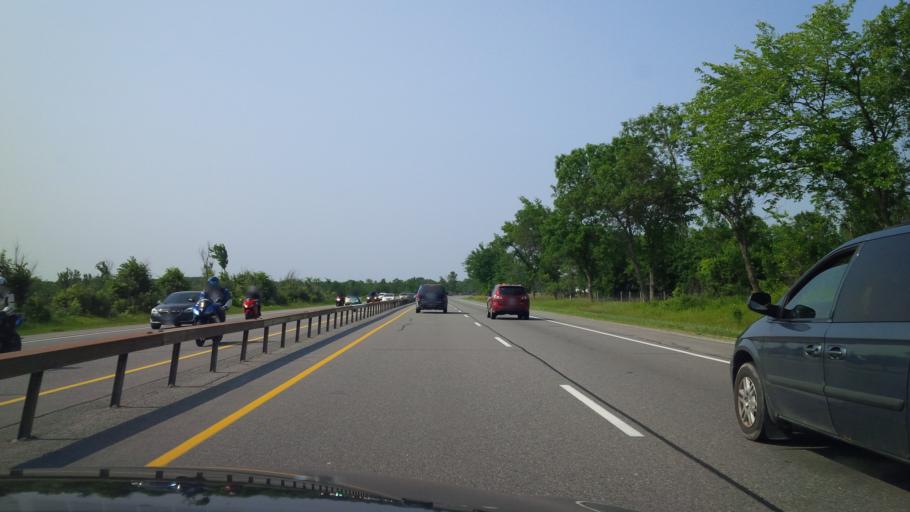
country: CA
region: Ontario
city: Orillia
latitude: 44.5140
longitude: -79.4692
